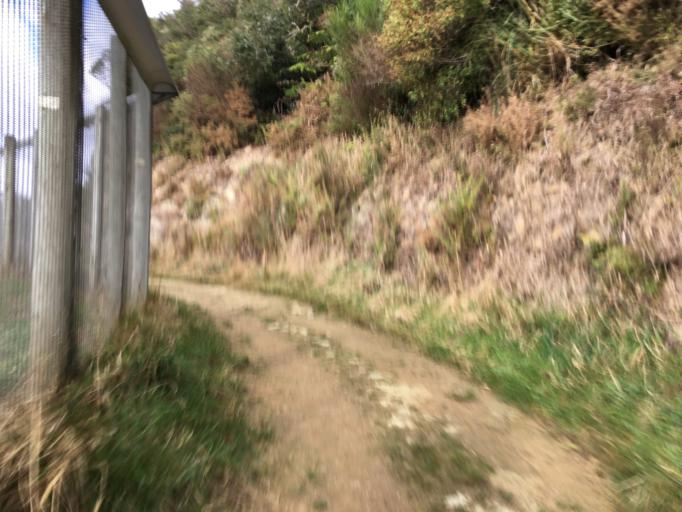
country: NZ
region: Wellington
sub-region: Wellington City
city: Brooklyn
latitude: -41.2971
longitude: 174.7391
